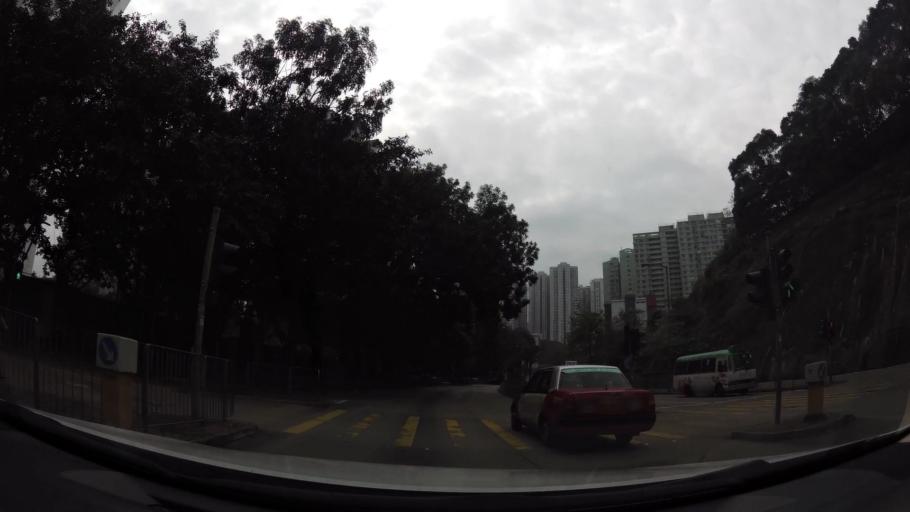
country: HK
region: Wanchai
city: Wan Chai
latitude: 22.2657
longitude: 114.2468
